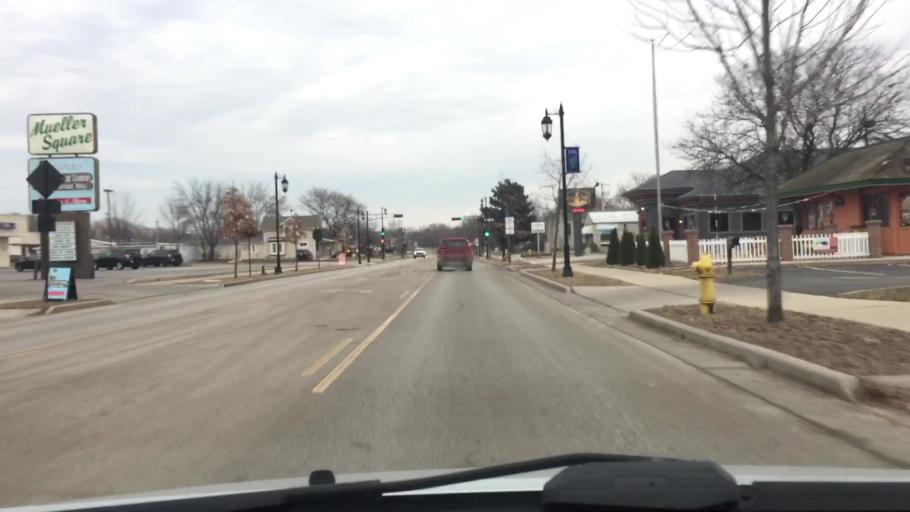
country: US
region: Wisconsin
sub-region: Waukesha County
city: Oconomowoc
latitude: 43.1090
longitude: -88.4934
